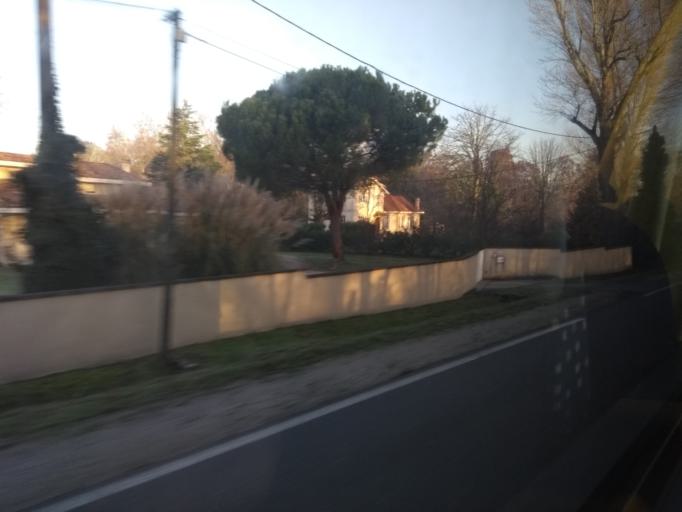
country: FR
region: Aquitaine
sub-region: Departement de la Gironde
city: Gradignan
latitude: 44.7631
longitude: -0.6209
